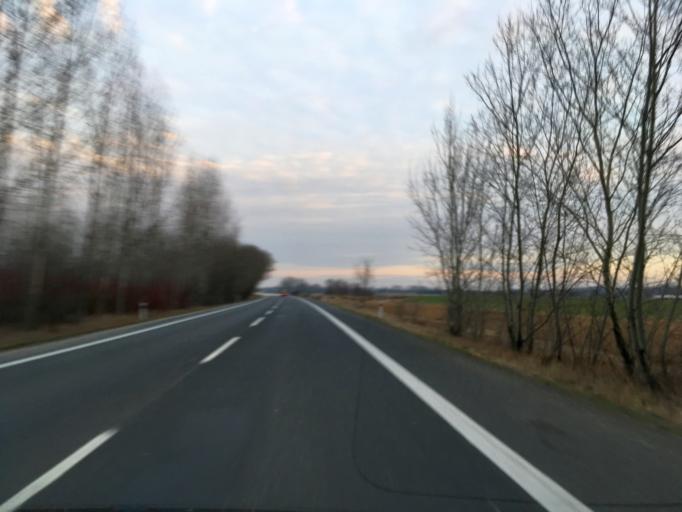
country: HU
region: Komarom-Esztergom
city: Acs
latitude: 47.7684
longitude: 17.9649
